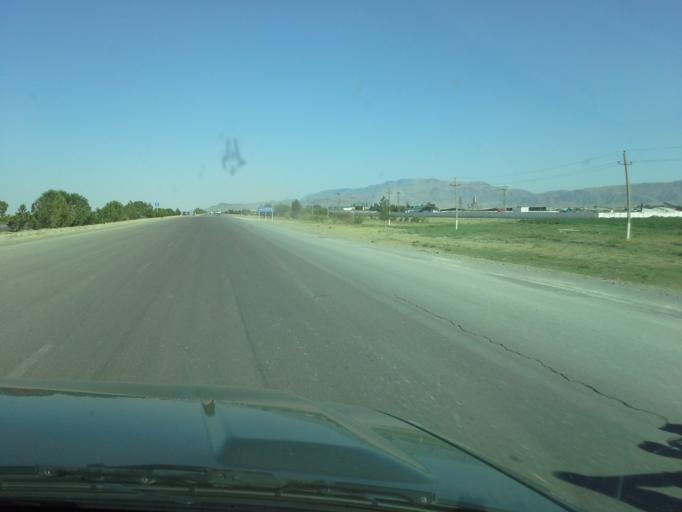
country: TM
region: Ahal
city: Baharly
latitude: 38.3263
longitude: 57.5869
